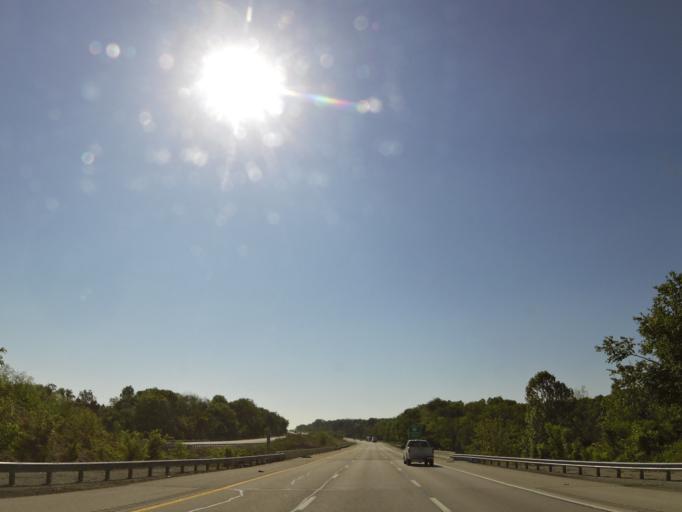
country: US
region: Kentucky
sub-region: Shelby County
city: Shelbyville
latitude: 38.1592
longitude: -85.0940
